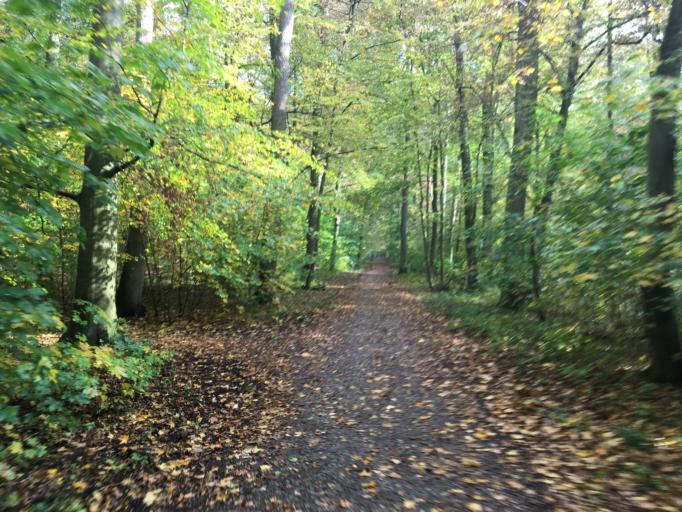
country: DE
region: Lower Saxony
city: Braunschweig
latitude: 52.3030
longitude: 10.5572
